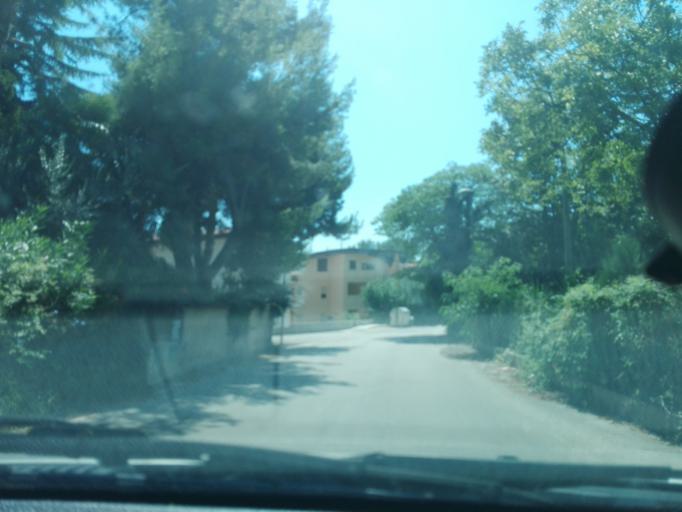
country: IT
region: Abruzzo
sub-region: Provincia di Pescara
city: Montesilvano Marina
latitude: 42.4956
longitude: 14.1602
